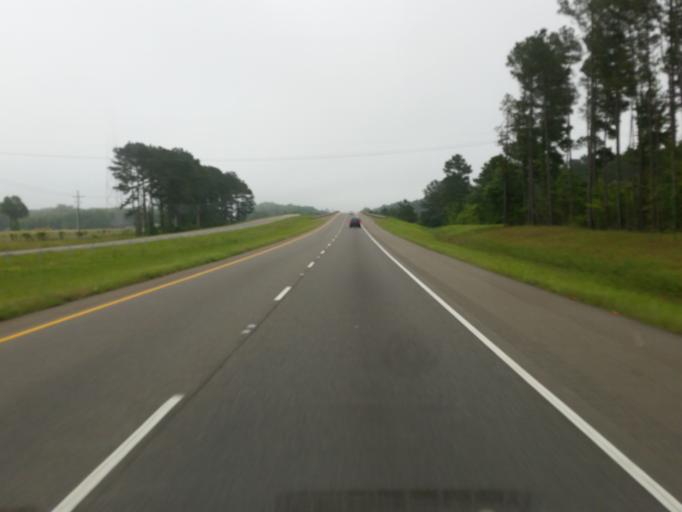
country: US
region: Louisiana
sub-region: Webster Parish
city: Sibley
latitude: 32.5822
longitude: -93.3959
